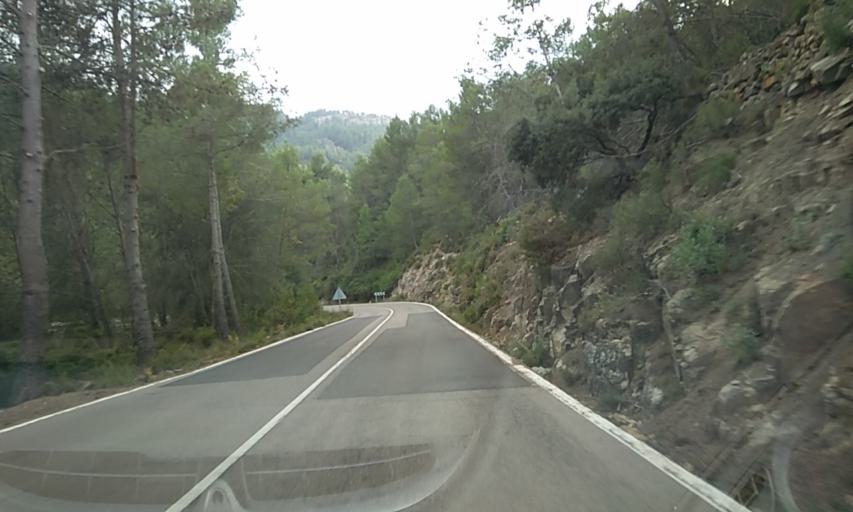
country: ES
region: Valencia
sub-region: Provincia de Castello
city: Puebla de Arenoso
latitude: 40.0876
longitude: -0.5659
